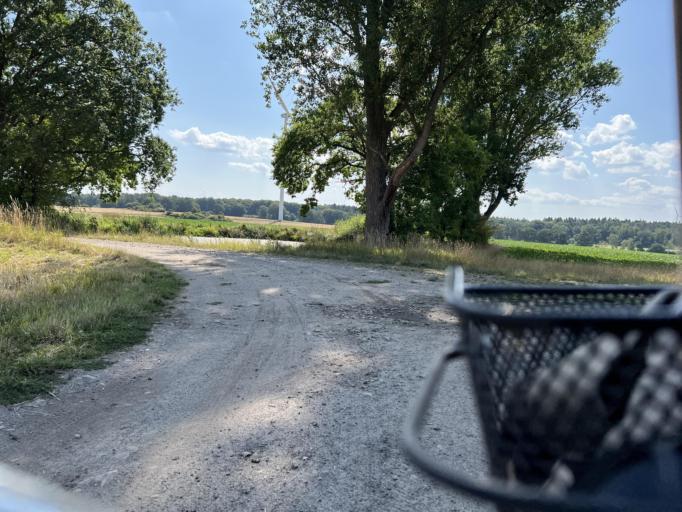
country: DE
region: Lower Saxony
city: Tosterglope
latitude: 53.1971
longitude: 10.7981
